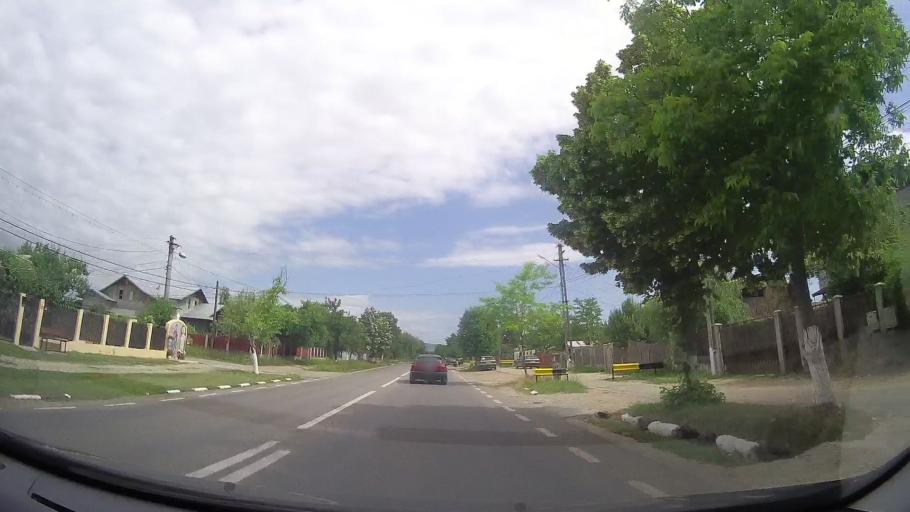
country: RO
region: Prahova
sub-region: Comuna Lipanesti
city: Lipanesti
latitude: 45.0585
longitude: 26.0209
